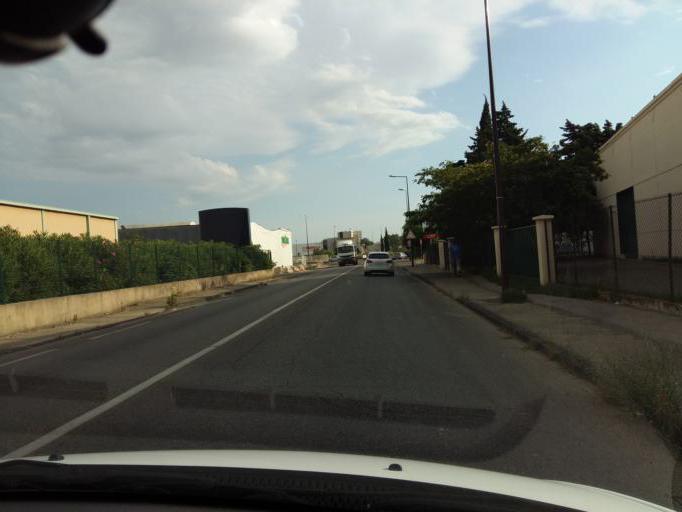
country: FR
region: Provence-Alpes-Cote d'Azur
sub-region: Departement du Vaucluse
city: Montfavet
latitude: 43.9367
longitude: 4.8489
